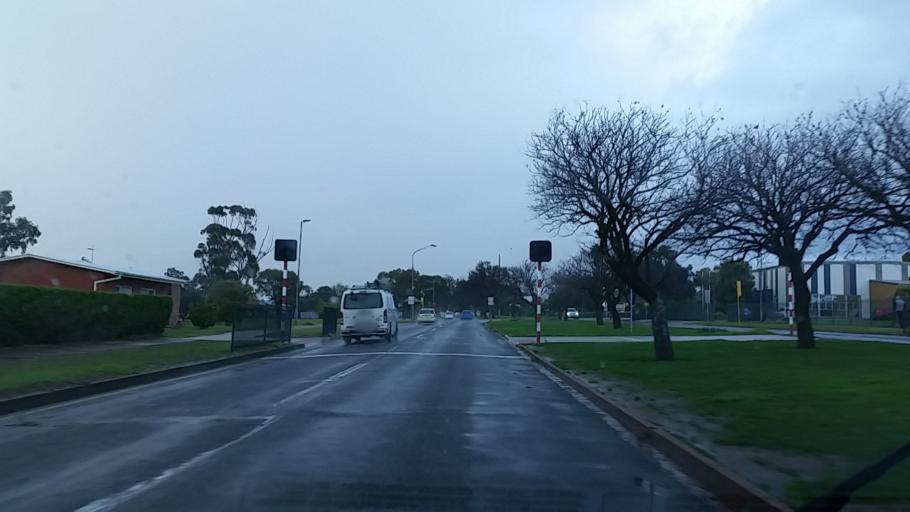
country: AU
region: South Australia
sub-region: Salisbury
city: Elizabeth
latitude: -34.7155
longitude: 138.6809
